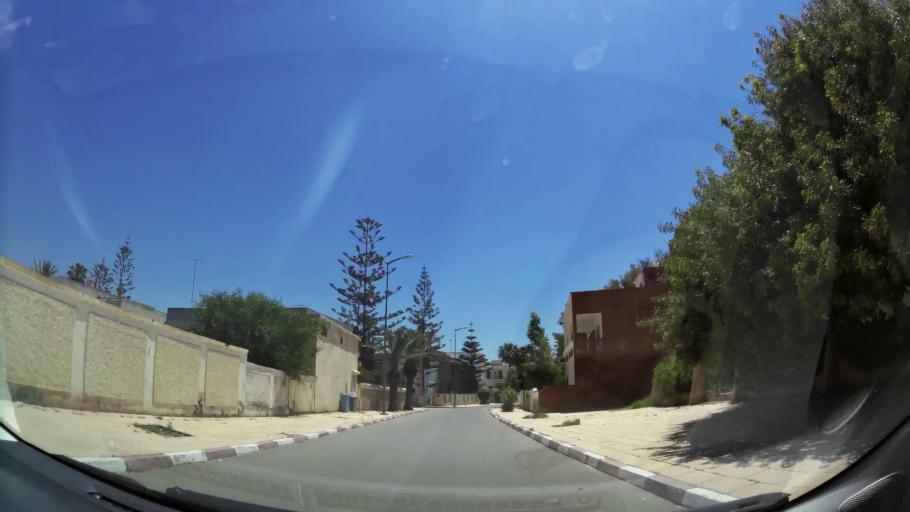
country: MA
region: Oriental
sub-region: Berkane-Taourirt
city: Madagh
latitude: 35.0871
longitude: -2.2347
